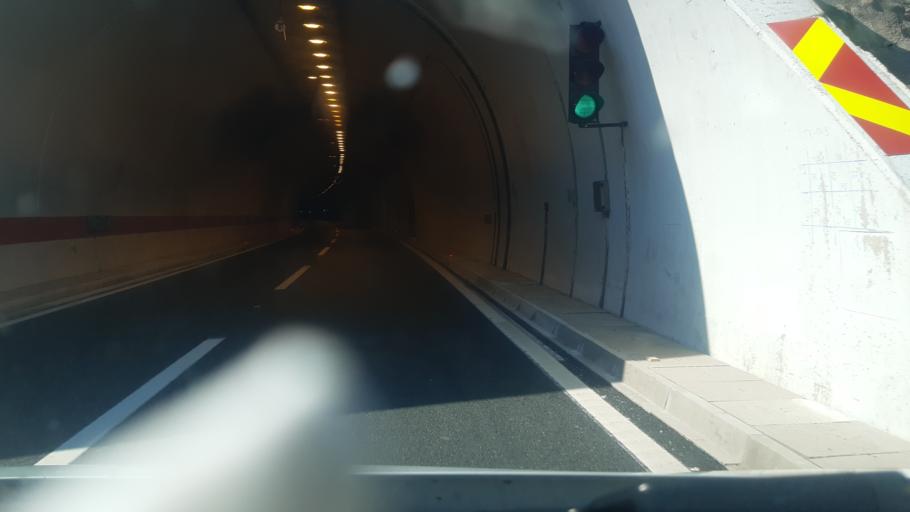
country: BA
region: Federation of Bosnia and Herzegovina
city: Ljubuski
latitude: 43.1281
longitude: 17.4840
